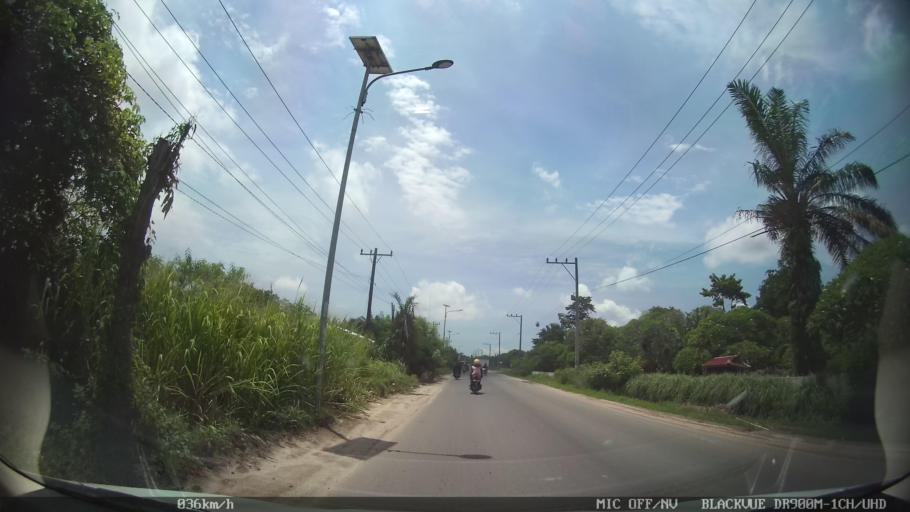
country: ID
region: North Sumatra
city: Perbaungan
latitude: 3.5283
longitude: 98.8878
